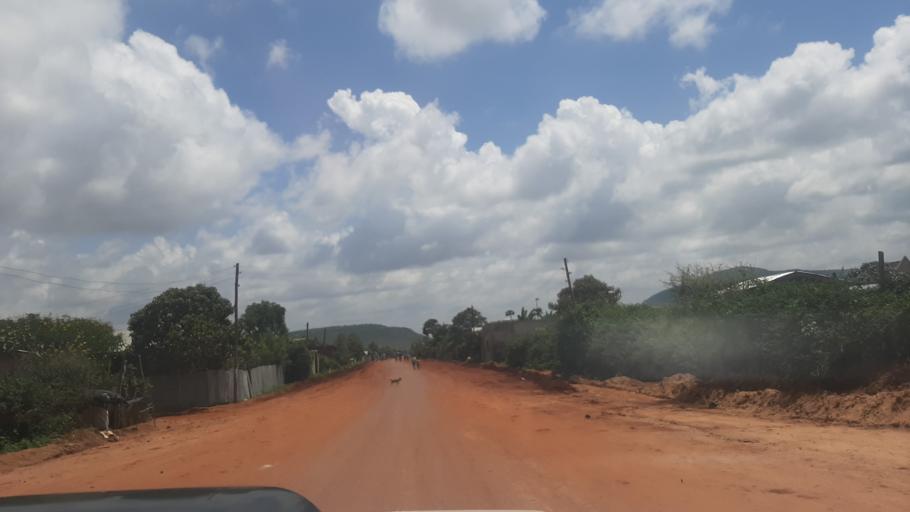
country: ET
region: Oromiya
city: Yabelo
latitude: 4.8935
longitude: 38.1028
